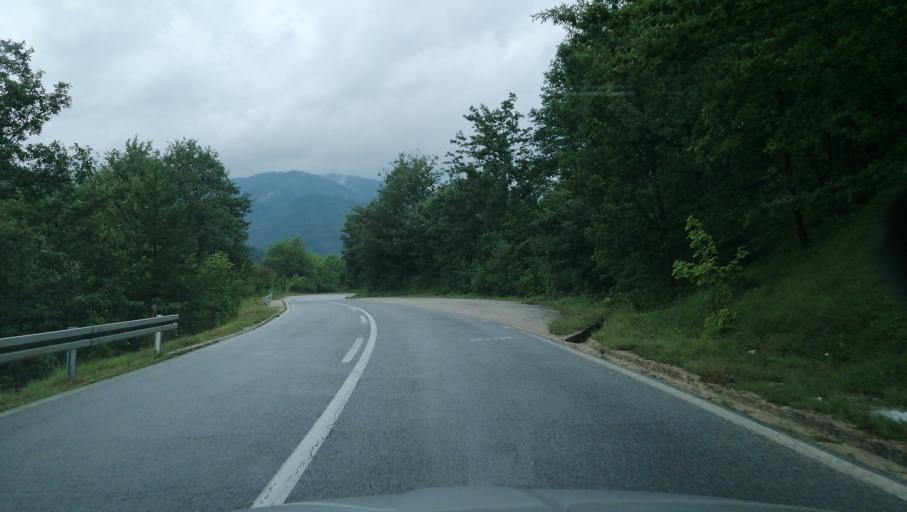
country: RS
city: Durici
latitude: 43.8059
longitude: 19.5108
